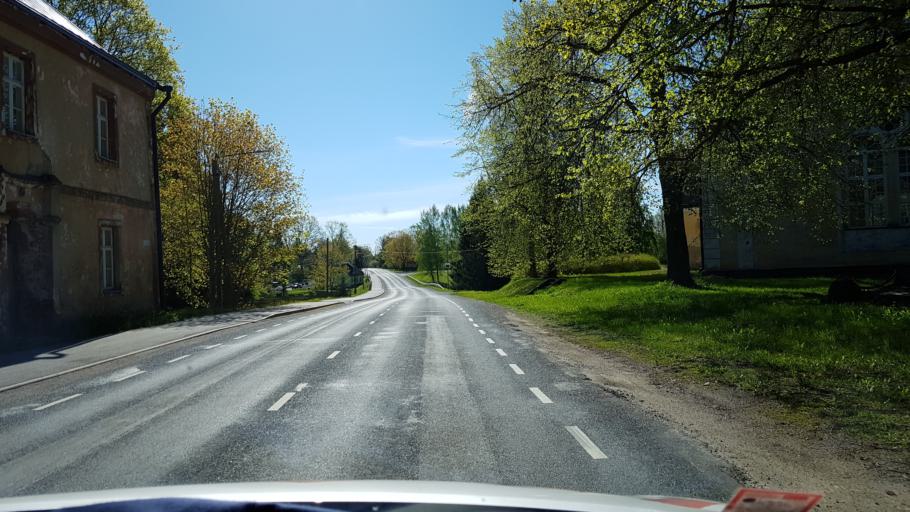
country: EE
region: Polvamaa
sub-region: Polva linn
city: Polva
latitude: 58.2847
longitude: 27.0415
